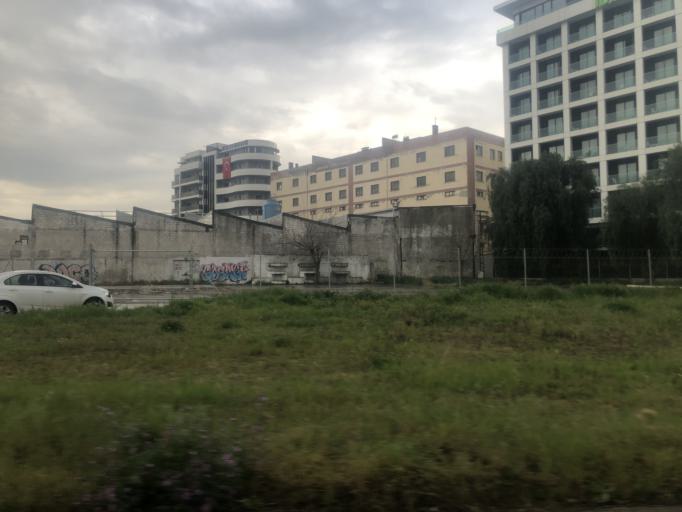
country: TR
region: Izmir
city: Bornova
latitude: 38.4513
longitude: 27.1917
